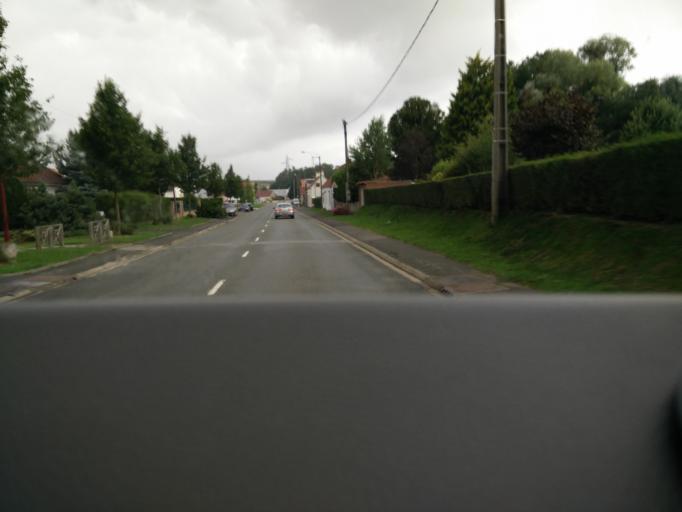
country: FR
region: Nord-Pas-de-Calais
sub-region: Departement du Pas-de-Calais
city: Aubigny-en-Artois
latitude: 50.3480
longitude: 2.5824
